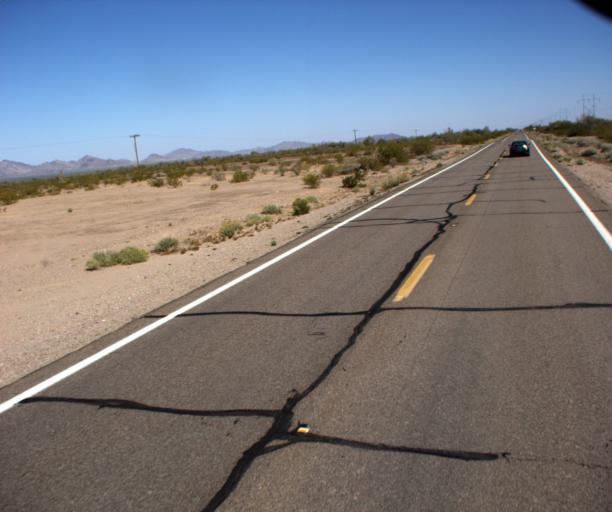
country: US
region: Arizona
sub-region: La Paz County
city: Quartzsite
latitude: 33.5082
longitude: -114.2170
